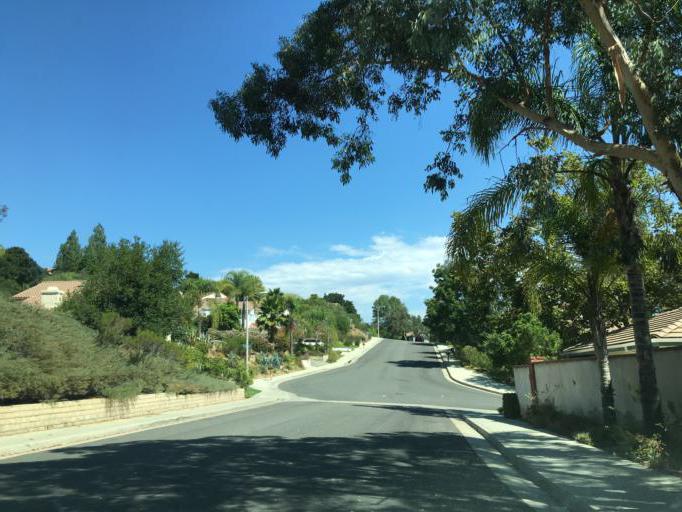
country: US
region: California
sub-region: Los Angeles County
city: Agoura
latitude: 34.1304
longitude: -118.7260
